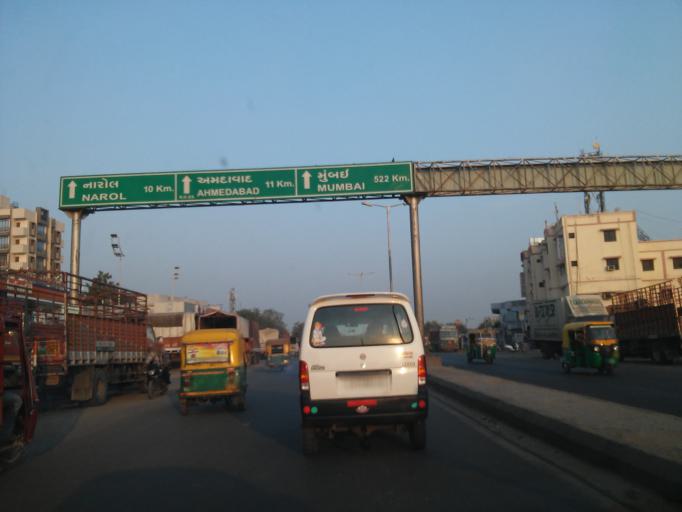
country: IN
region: Gujarat
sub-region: Ahmadabad
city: Sarkhej
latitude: 22.9881
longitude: 72.5063
